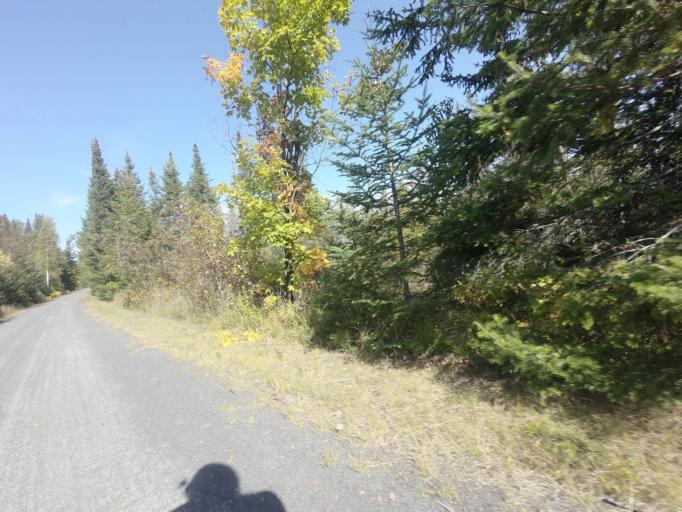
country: CA
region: Quebec
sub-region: Laurentides
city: Sainte-Agathe-des-Monts
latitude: 46.0859
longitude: -74.3405
